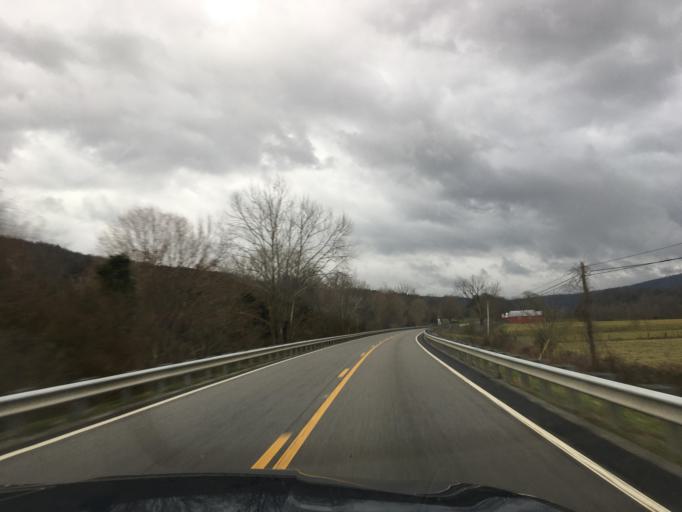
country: US
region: Tennessee
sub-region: Cumberland County
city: Lake Tansi
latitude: 35.8598
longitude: -84.9203
